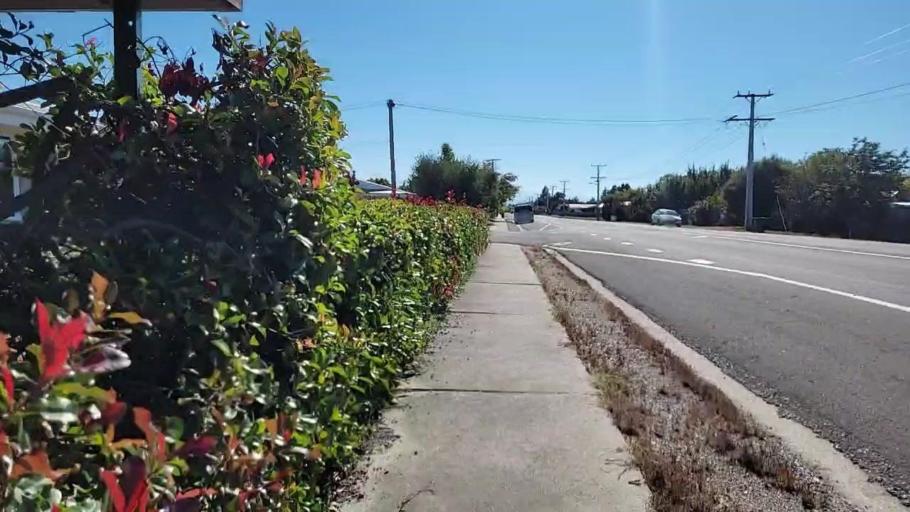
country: NZ
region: Otago
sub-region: Queenstown-Lakes District
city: Wanaka
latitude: -45.1044
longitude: 169.5948
